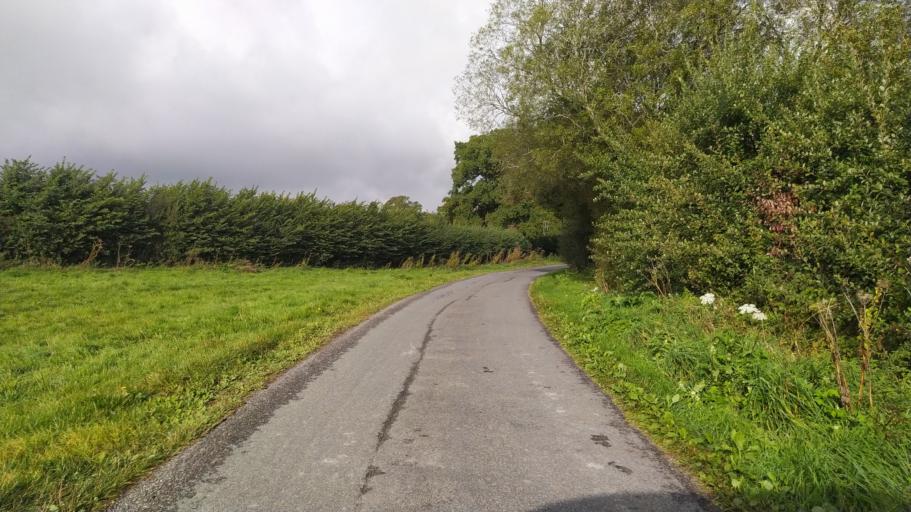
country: GB
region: England
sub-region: Dorset
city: Shaftesbury
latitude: 51.0397
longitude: -2.1508
